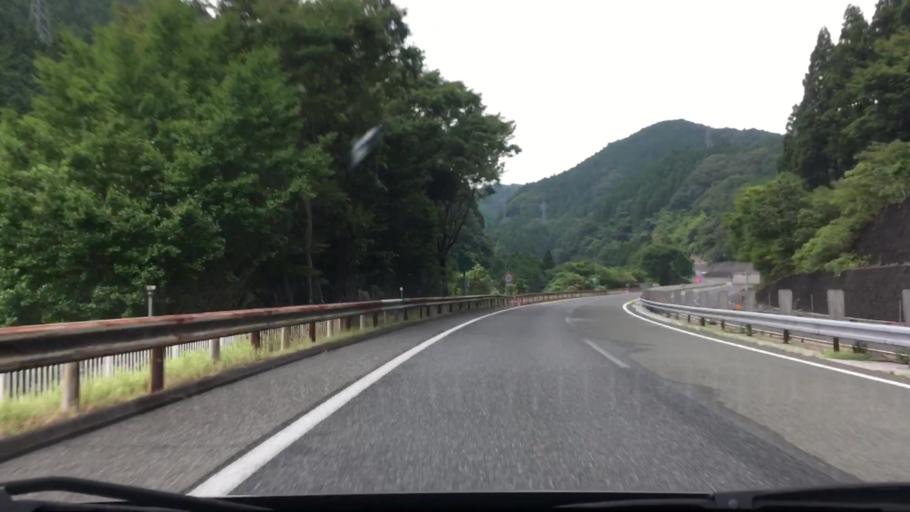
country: JP
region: Okayama
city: Niimi
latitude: 35.0163
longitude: 133.4292
